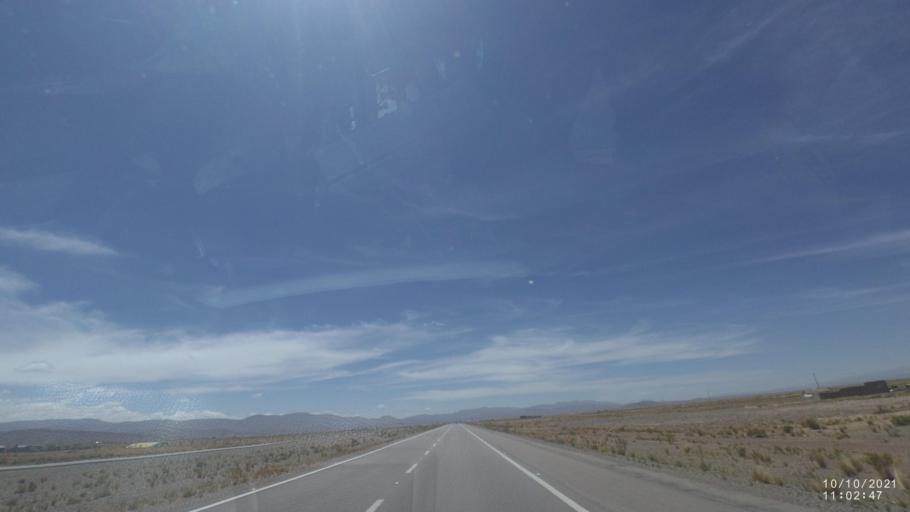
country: BO
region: La Paz
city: Colquiri
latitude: -17.6525
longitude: -67.1571
